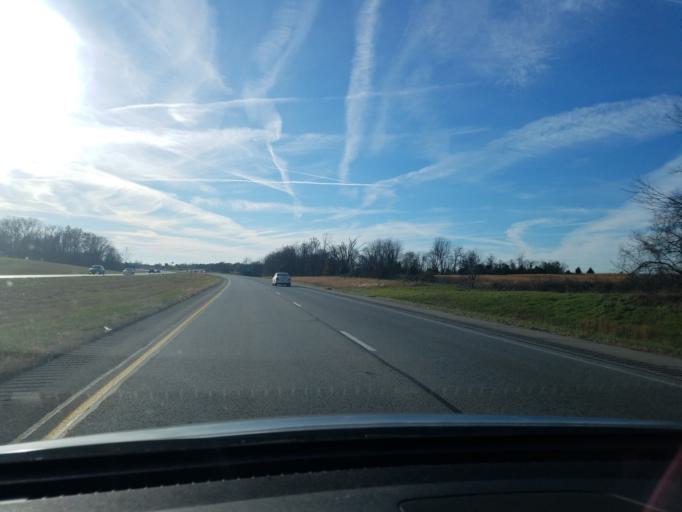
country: US
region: Indiana
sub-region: Floyd County
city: Georgetown
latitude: 38.2686
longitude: -85.9930
